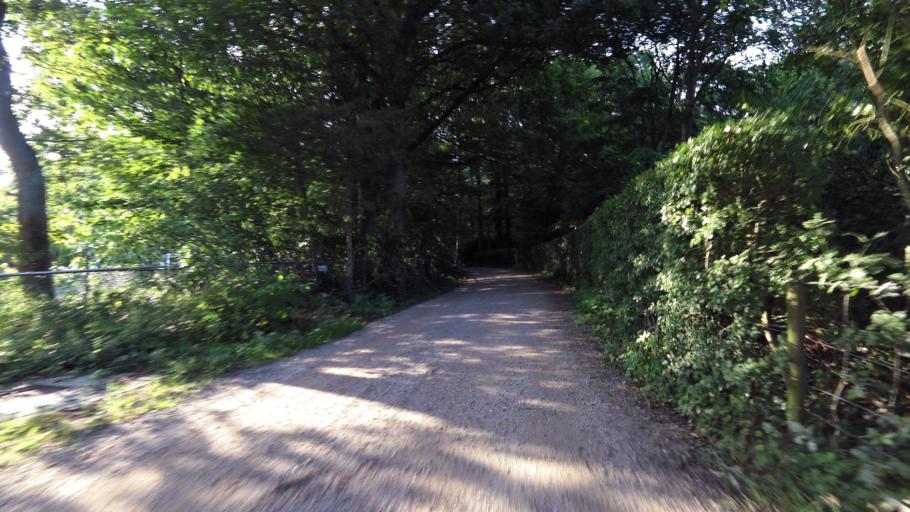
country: NL
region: Utrecht
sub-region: Gemeente Soest
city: Soest
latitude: 52.1713
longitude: 5.2505
